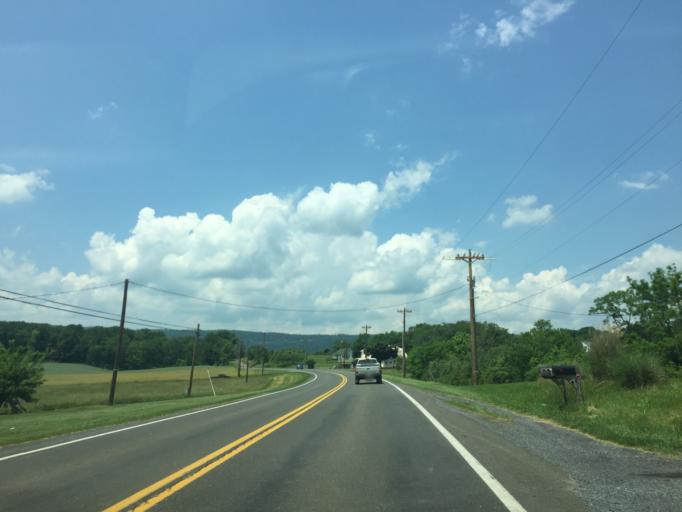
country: US
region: Virginia
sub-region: Shenandoah County
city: Strasburg
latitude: 39.0309
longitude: -78.3706
